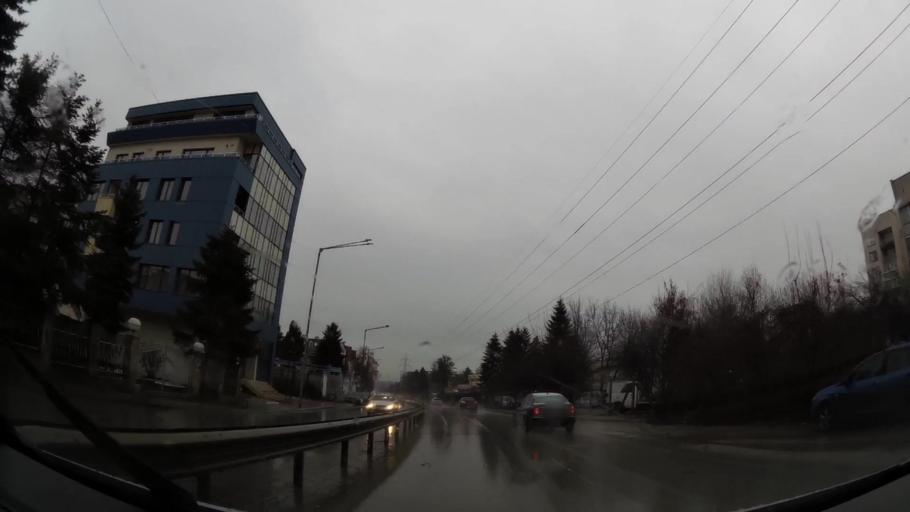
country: BG
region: Sofia-Capital
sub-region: Stolichna Obshtina
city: Sofia
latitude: 42.6473
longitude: 23.3353
